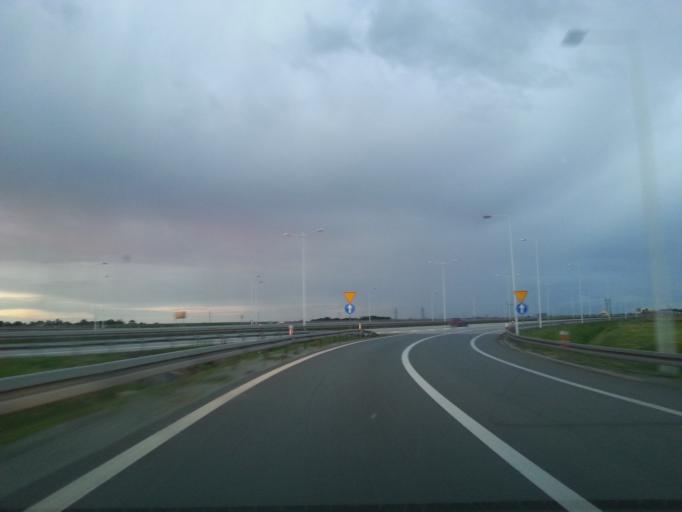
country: PL
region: Lower Silesian Voivodeship
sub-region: Powiat wroclawski
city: Bielany Wroclawskie
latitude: 51.0453
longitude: 16.9386
